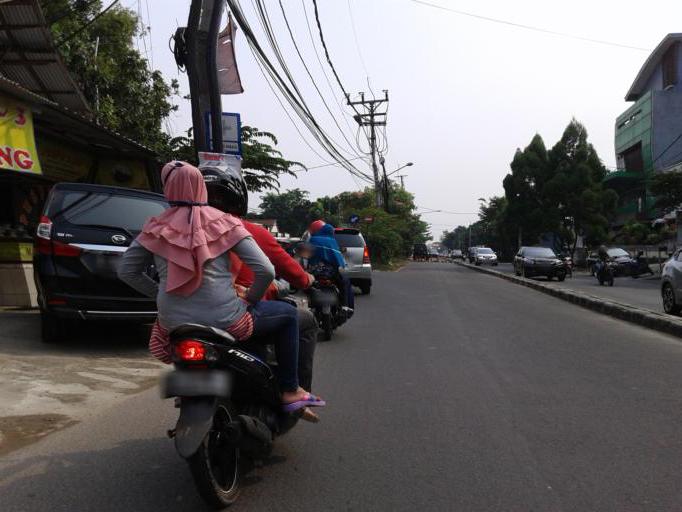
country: ID
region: West Java
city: Pamulang
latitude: -6.3406
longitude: 106.7798
